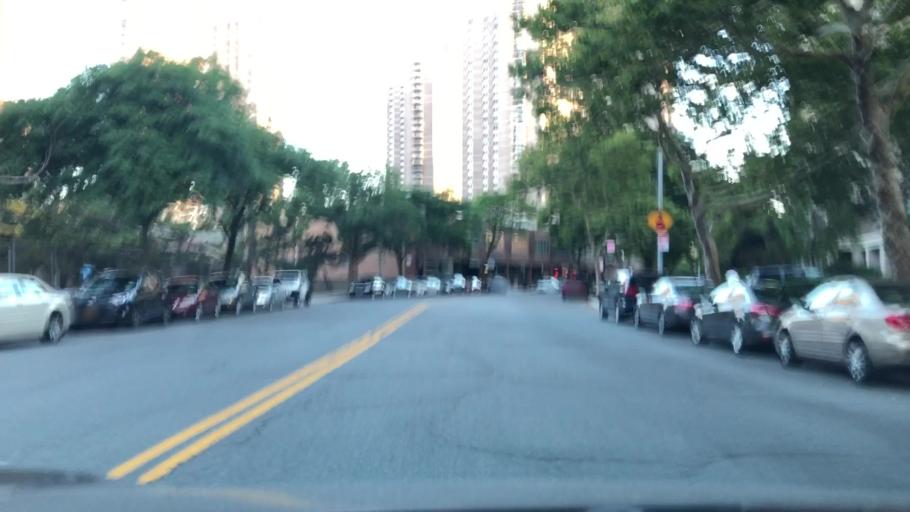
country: US
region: New York
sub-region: Bronx
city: Eastchester
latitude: 40.8779
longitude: -73.8296
